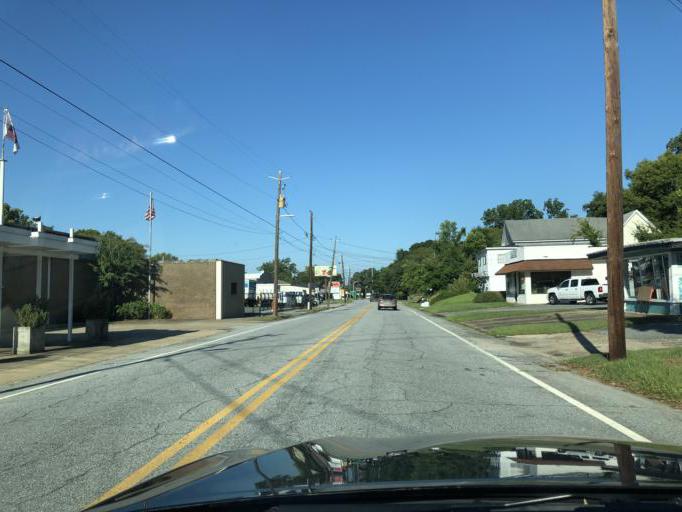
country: US
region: Georgia
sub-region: Muscogee County
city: Columbus
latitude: 32.4777
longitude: -84.9762
